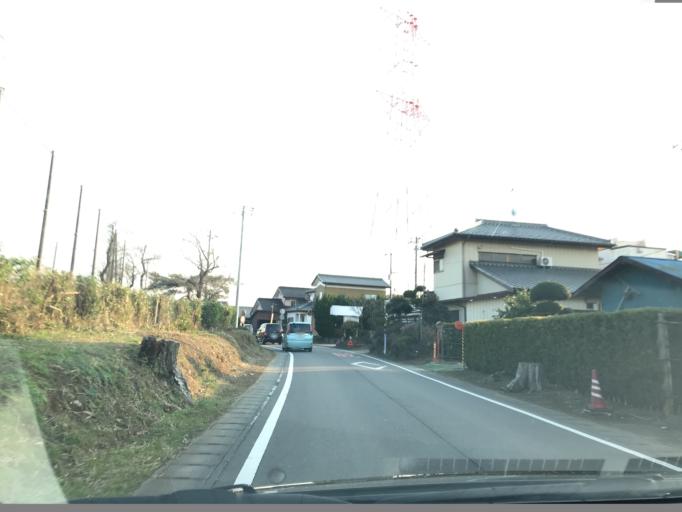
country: JP
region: Ibaraki
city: Ushiku
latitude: 36.0237
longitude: 140.0740
